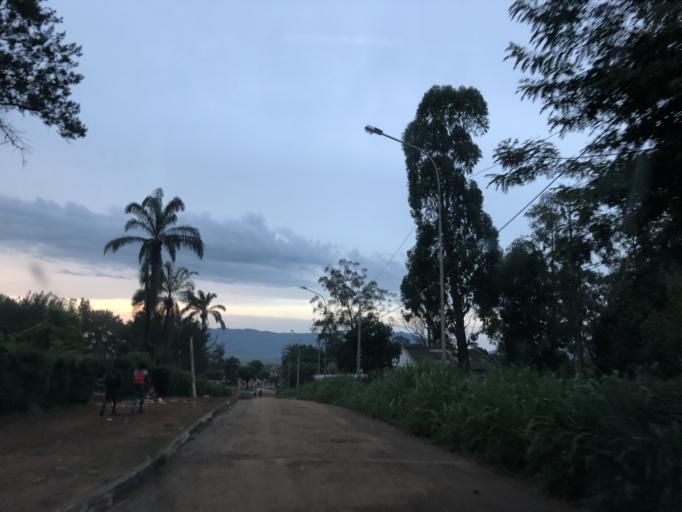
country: AO
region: Cuanza Sul
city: Uacu Cungo
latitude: -11.3677
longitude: 15.1173
